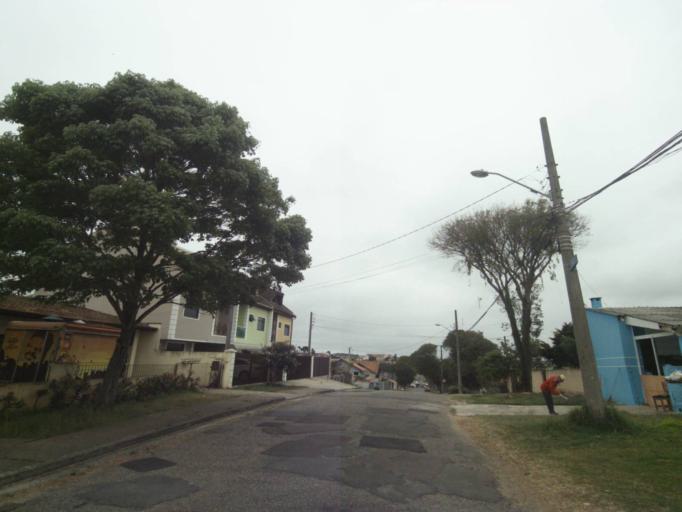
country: BR
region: Parana
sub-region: Pinhais
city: Pinhais
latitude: -25.4764
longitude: -49.2353
